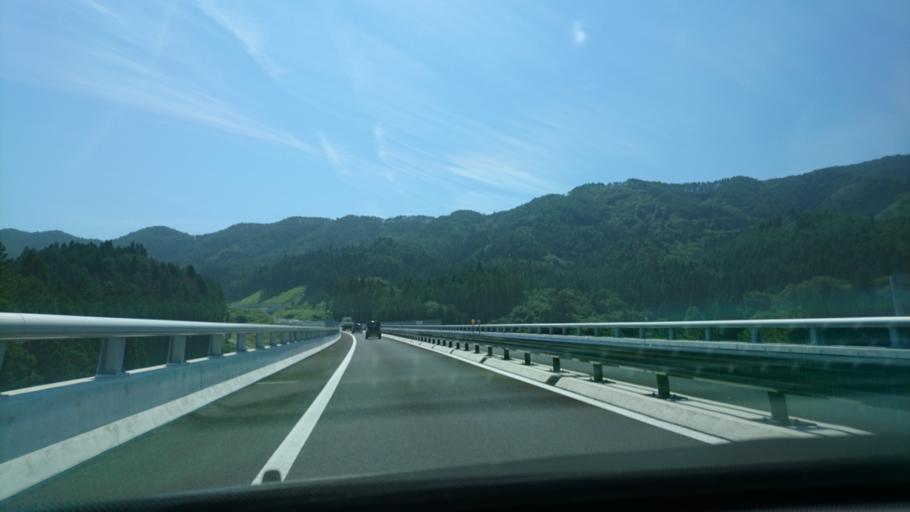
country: JP
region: Iwate
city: Ofunato
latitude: 38.9924
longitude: 141.6131
